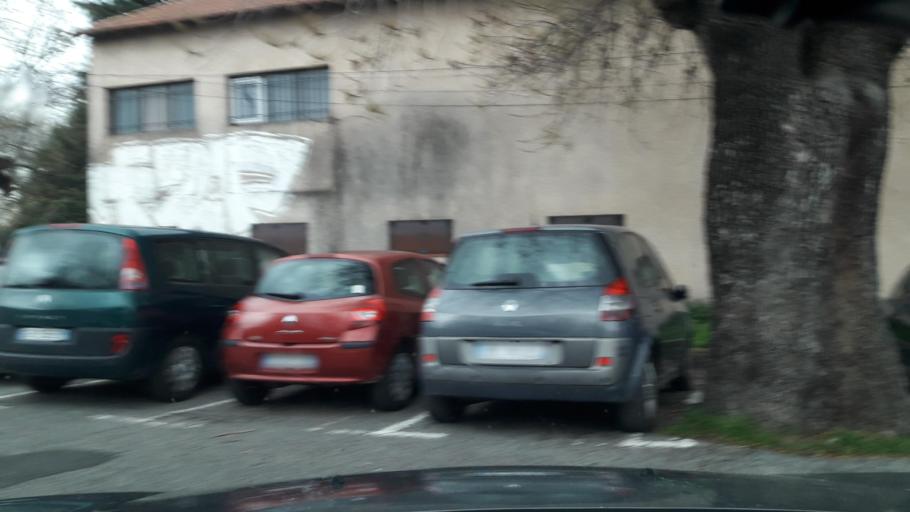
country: FR
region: Provence-Alpes-Cote d'Azur
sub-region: Departement du Var
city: Frejus
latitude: 43.4307
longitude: 6.7380
